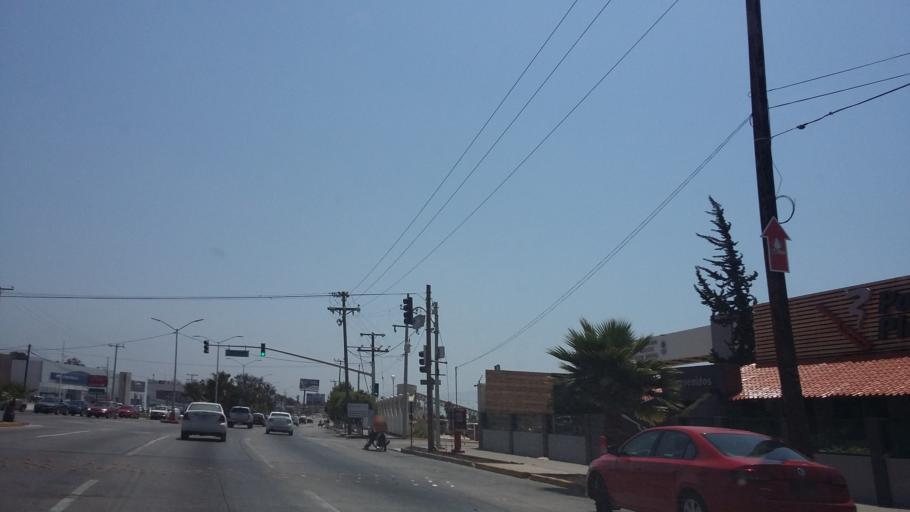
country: MX
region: Baja California
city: Ensenada
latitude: 31.8501
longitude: -116.6150
